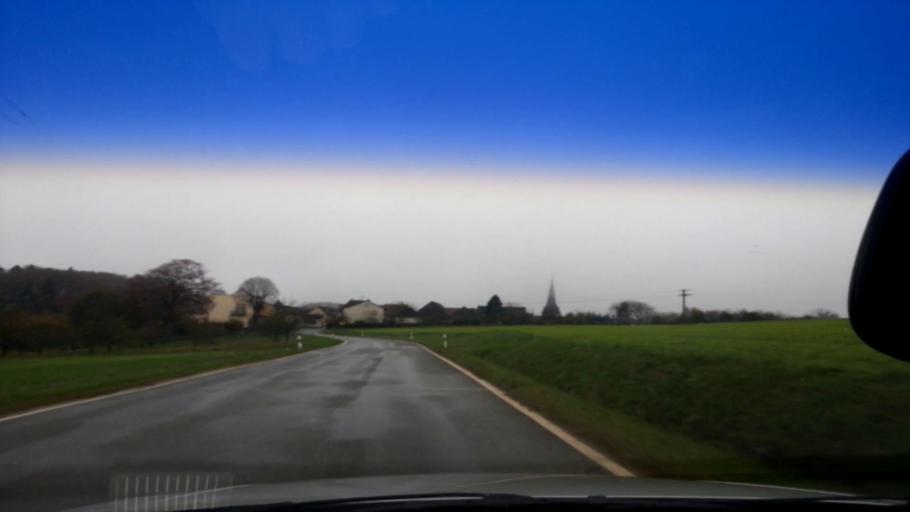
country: DE
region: Bavaria
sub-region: Upper Franconia
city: Wattendorf
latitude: 50.0340
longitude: 11.1313
